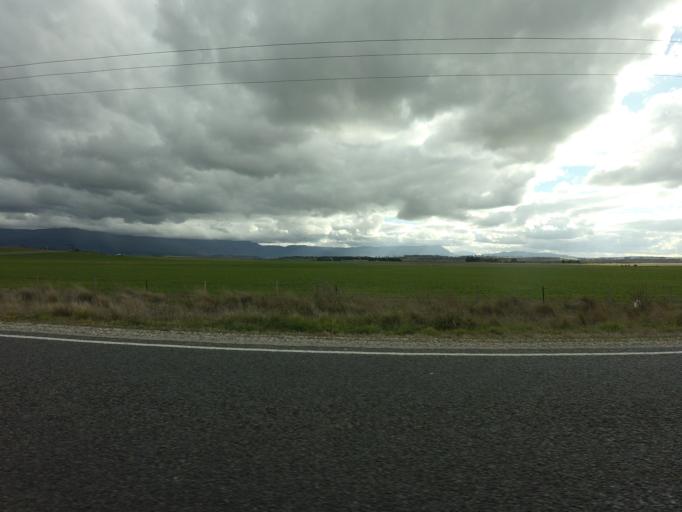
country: AU
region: Tasmania
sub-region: Northern Midlands
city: Longford
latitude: -41.7526
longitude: 147.0824
